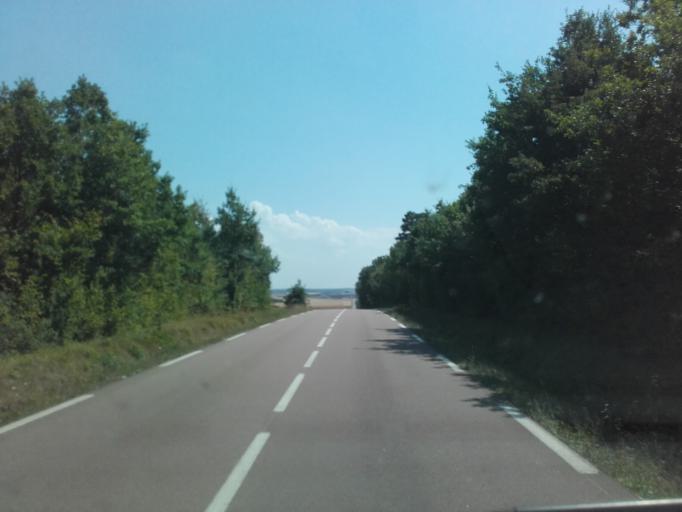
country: FR
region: Bourgogne
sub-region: Departement de l'Yonne
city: Joux-la-Ville
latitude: 47.7047
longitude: 3.8572
